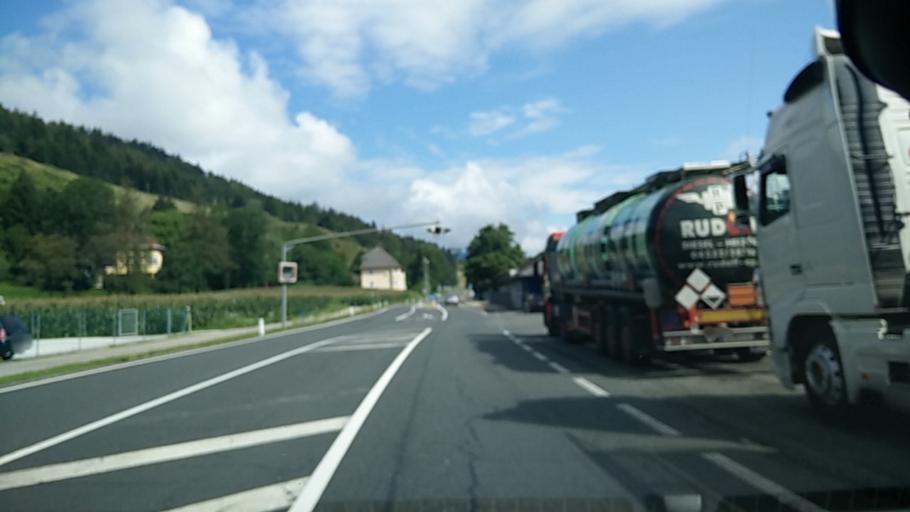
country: AT
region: Carinthia
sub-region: Politischer Bezirk Sankt Veit an der Glan
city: Bruckl
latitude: 46.7330
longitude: 14.5272
